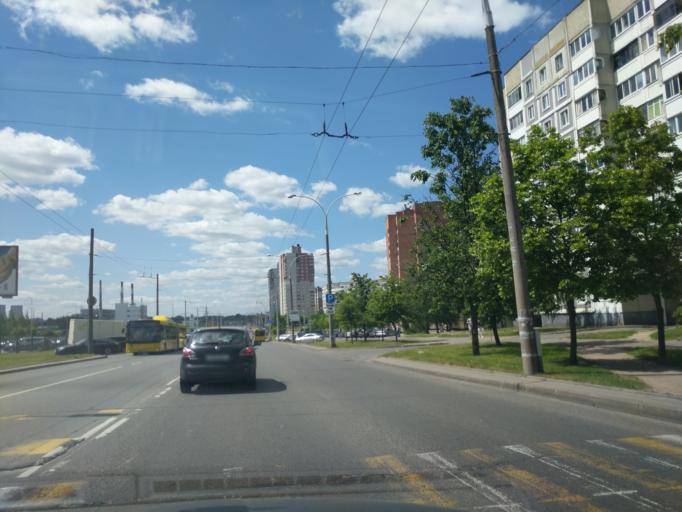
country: BY
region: Minsk
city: Novoye Medvezhino
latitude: 53.8824
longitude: 27.4382
